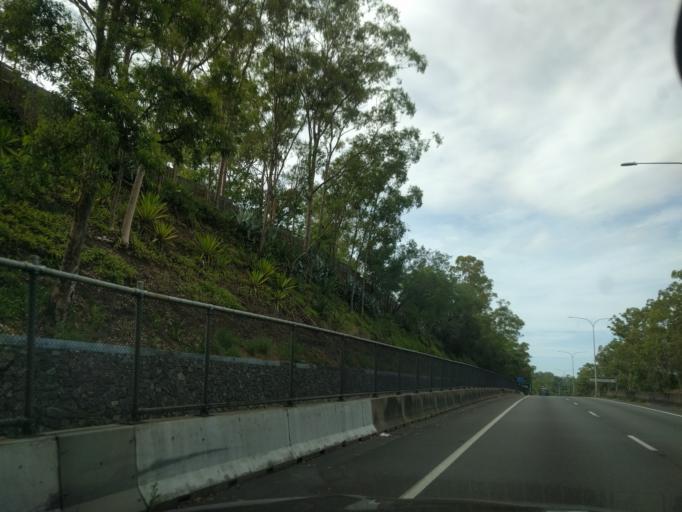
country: AU
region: Queensland
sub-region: Brisbane
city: Kenmore Hills
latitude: -27.5113
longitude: 152.9583
